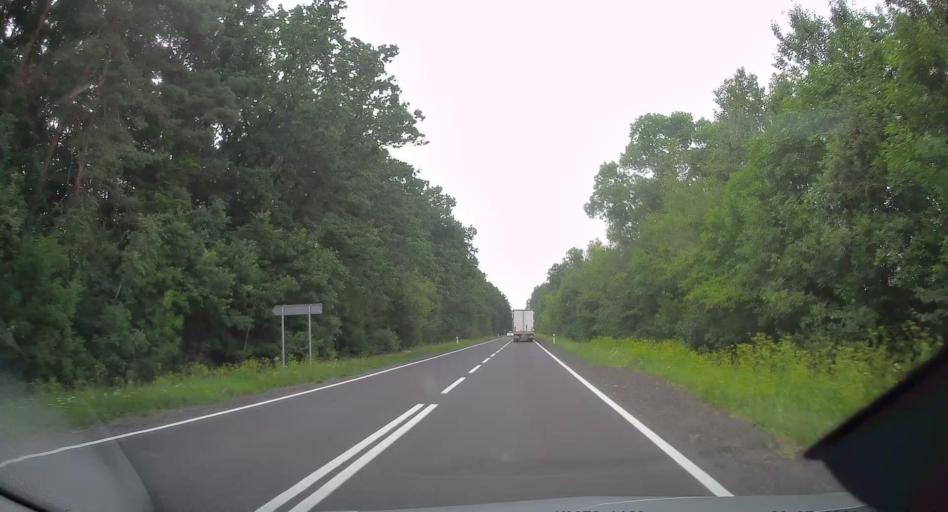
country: PL
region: Silesian Voivodeship
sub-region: Powiat czestochowski
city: Klomnice
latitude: 50.9487
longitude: 19.3965
